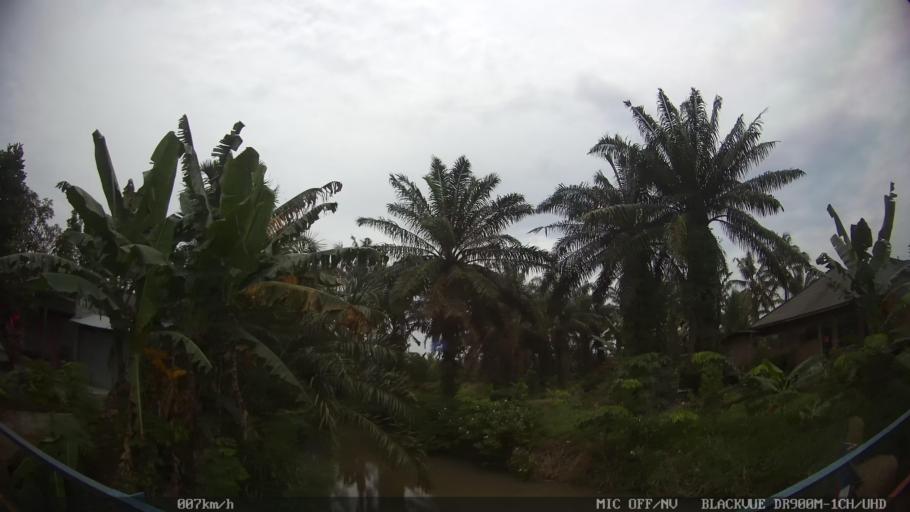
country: ID
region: North Sumatra
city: Binjai
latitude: 3.6408
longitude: 98.5517
